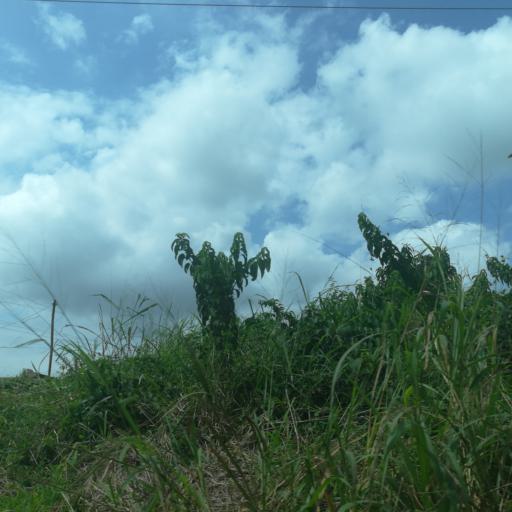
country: NG
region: Lagos
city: Ejirin
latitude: 6.6503
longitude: 3.7079
